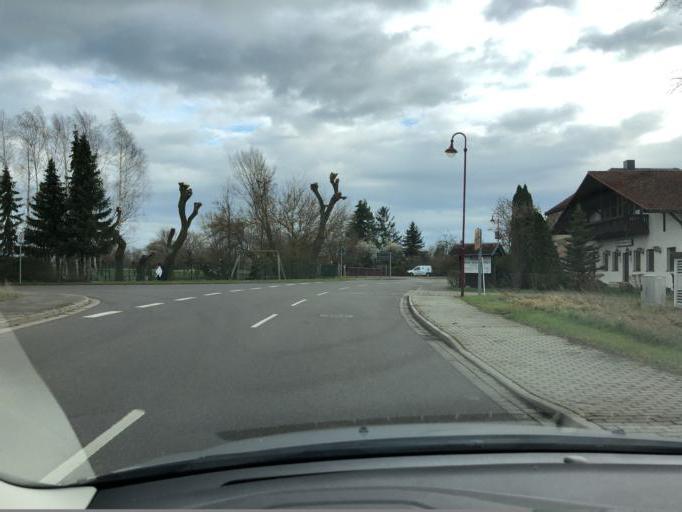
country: DE
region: Saxony
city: Markranstadt
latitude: 51.2745
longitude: 12.2061
